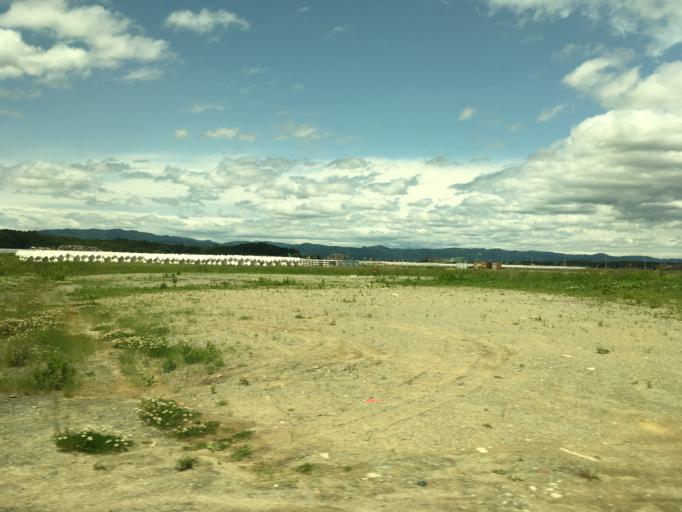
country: JP
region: Fukushima
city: Namie
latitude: 37.4768
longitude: 141.0372
